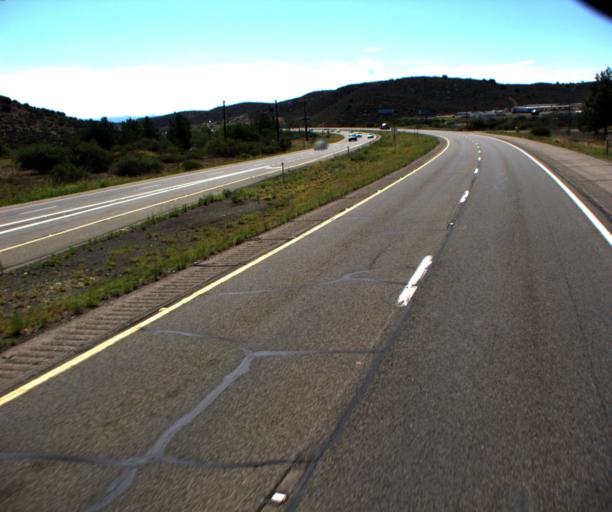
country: US
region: Arizona
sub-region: Yavapai County
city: Mayer
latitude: 34.3871
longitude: -112.2191
